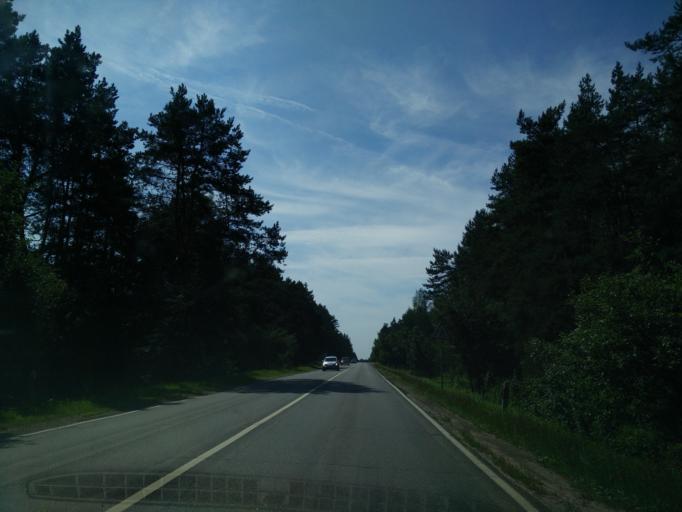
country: LT
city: Nemencine
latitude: 54.7952
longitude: 25.3924
